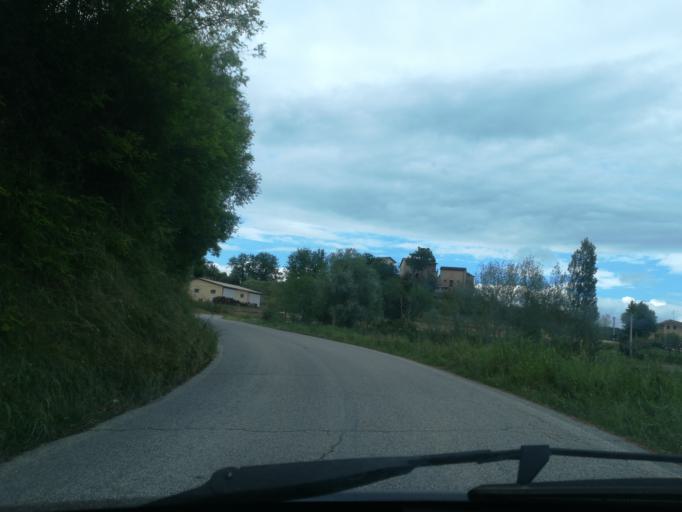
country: IT
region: The Marches
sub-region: Province of Fermo
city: Montefortino
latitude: 42.9348
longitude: 13.3729
